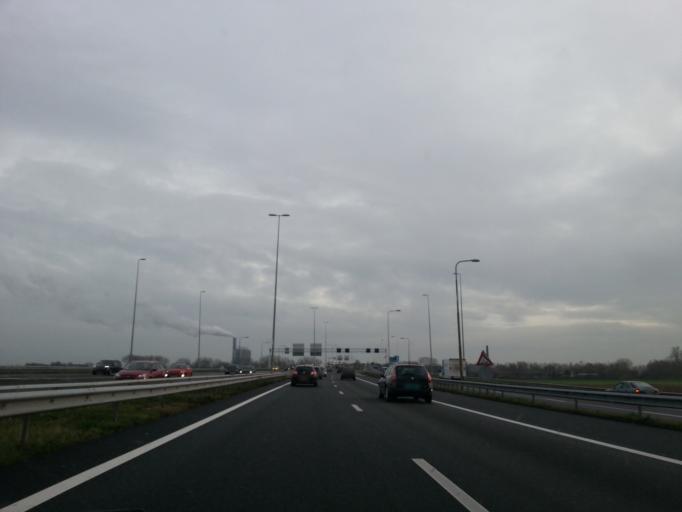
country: NL
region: Gelderland
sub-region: Gemeente Rheden
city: Velp
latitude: 51.9793
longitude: 5.9836
